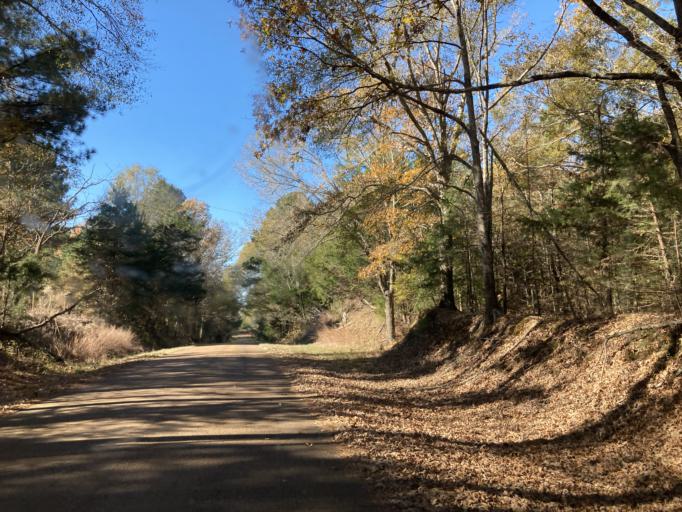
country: US
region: Mississippi
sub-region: Hinds County
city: Lynchburg
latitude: 32.5959
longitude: -90.4956
